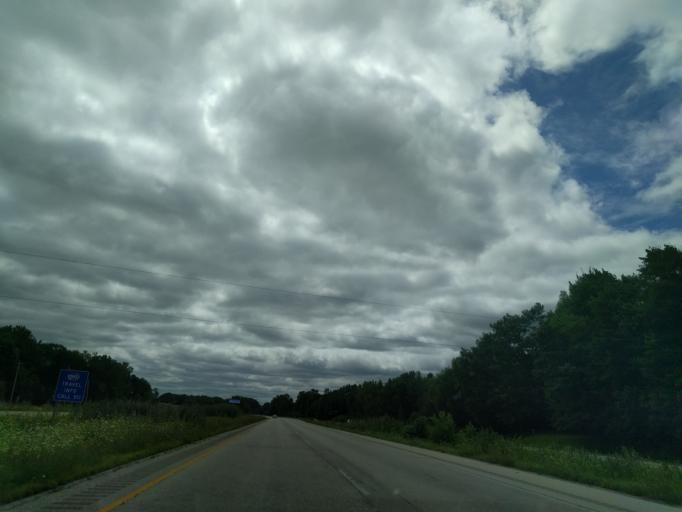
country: US
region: Wisconsin
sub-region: Brown County
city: Suamico
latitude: 44.6499
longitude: -88.0501
